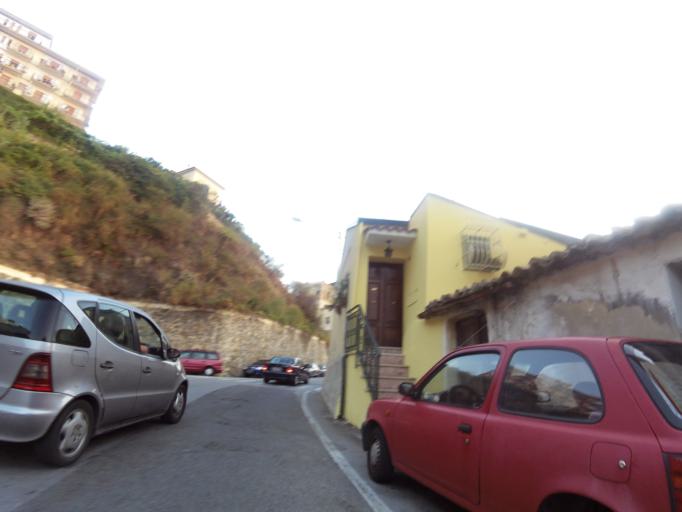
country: IT
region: Calabria
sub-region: Provincia di Vibo-Valentia
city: Pizzo
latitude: 38.7369
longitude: 16.1655
